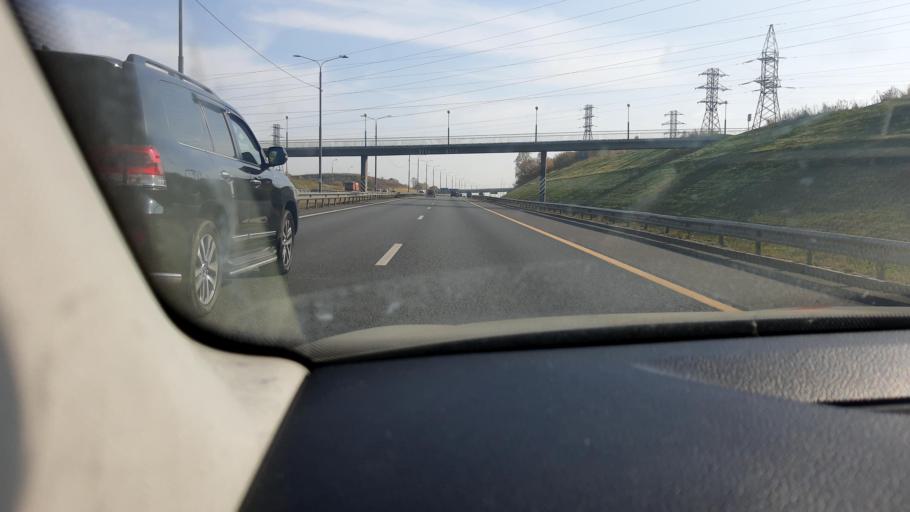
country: RU
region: Moskovskaya
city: Stupino
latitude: 54.8136
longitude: 38.0604
